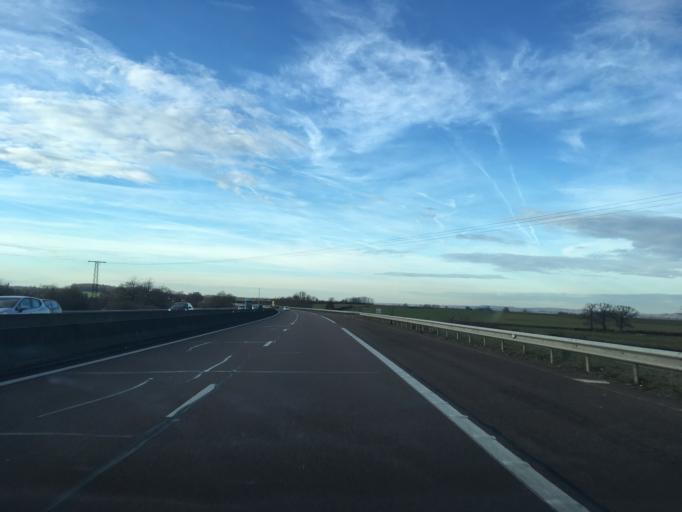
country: FR
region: Bourgogne
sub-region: Departement de la Cote-d'Or
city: Semur-en-Auxois
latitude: 47.4641
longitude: 4.2482
